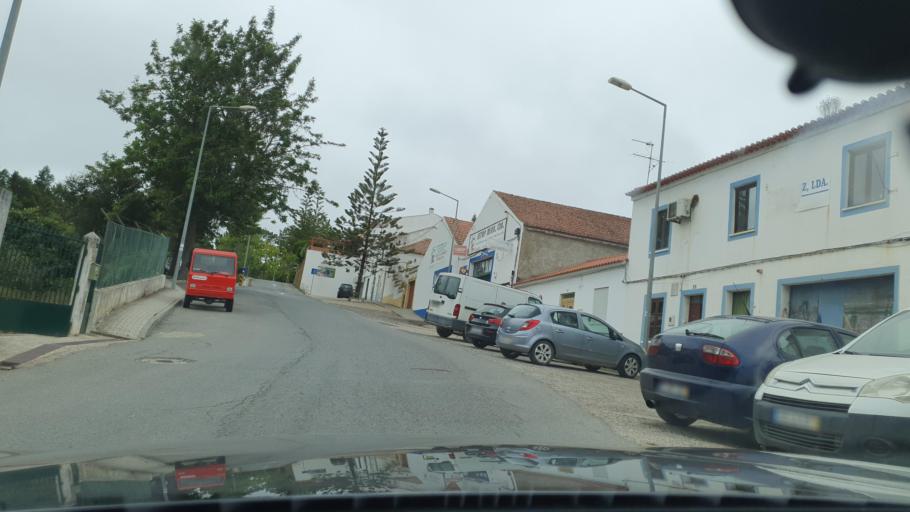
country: PT
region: Beja
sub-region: Odemira
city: Sao Teotonio
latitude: 37.5087
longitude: -8.7071
